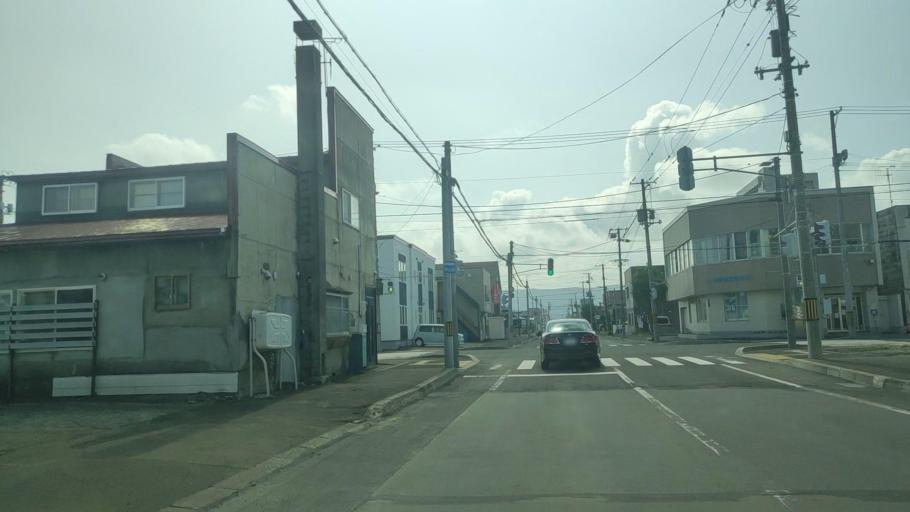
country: JP
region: Hokkaido
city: Shimo-furano
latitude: 43.3457
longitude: 142.3860
